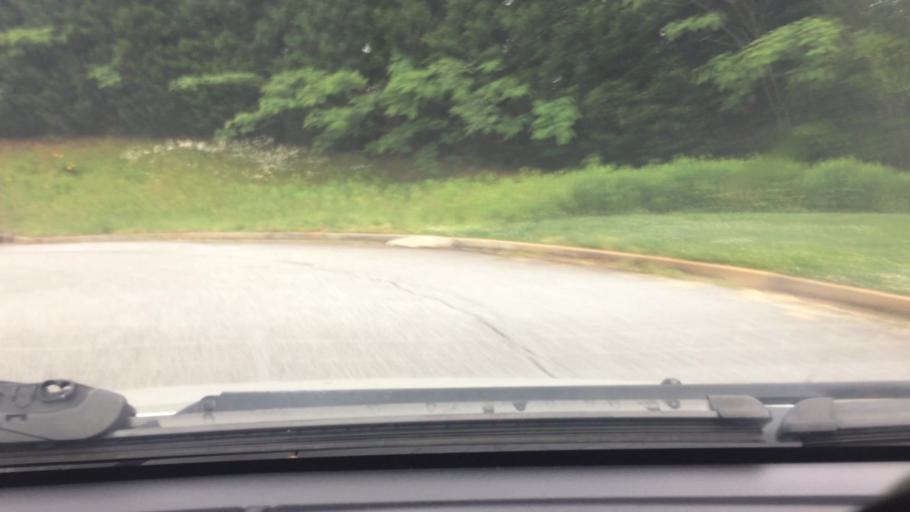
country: US
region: South Carolina
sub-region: Spartanburg County
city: Valley Falls
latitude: 35.0018
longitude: -81.9376
